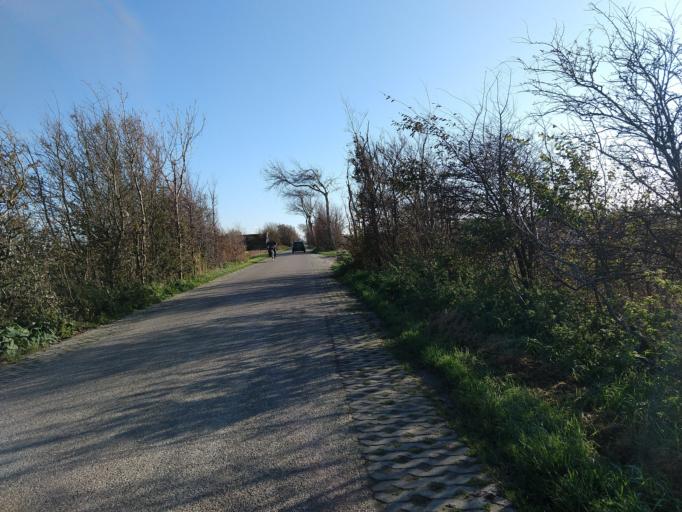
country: NL
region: Zeeland
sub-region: Gemeente Vlissingen
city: Vlissingen
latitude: 51.5404
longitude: 3.4750
